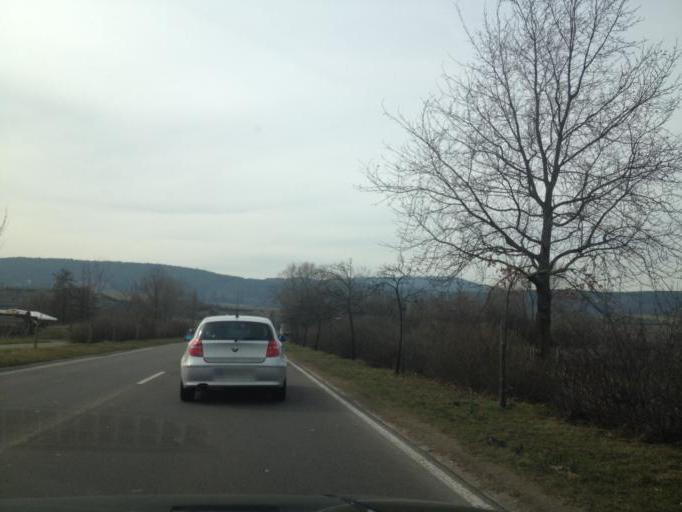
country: DE
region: Rheinland-Pfalz
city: Bad Duerkheim
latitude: 49.4703
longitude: 8.1818
